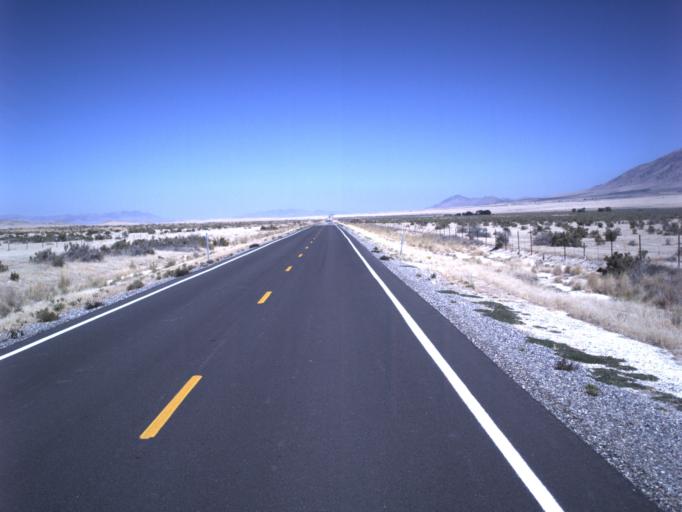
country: US
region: Utah
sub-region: Tooele County
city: Grantsville
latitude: 40.3193
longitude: -112.7437
